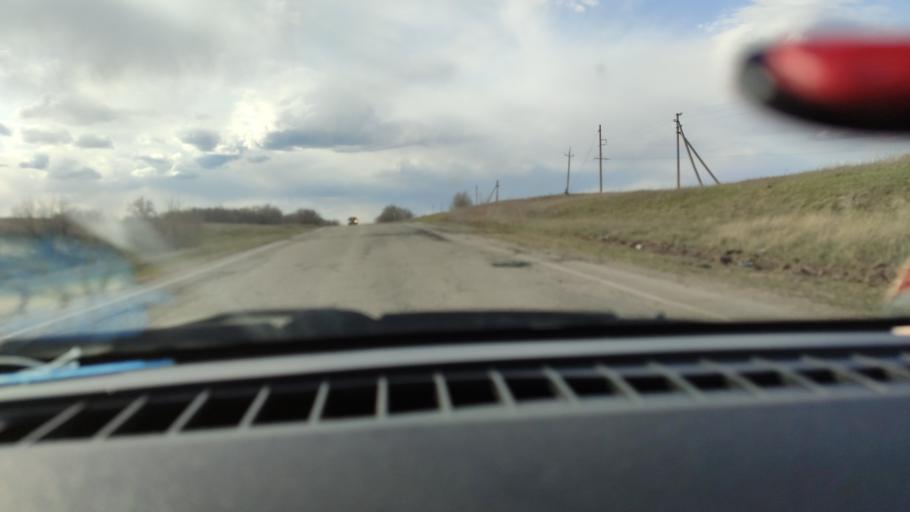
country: RU
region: Saratov
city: Rovnoye
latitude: 51.0509
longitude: 46.0422
